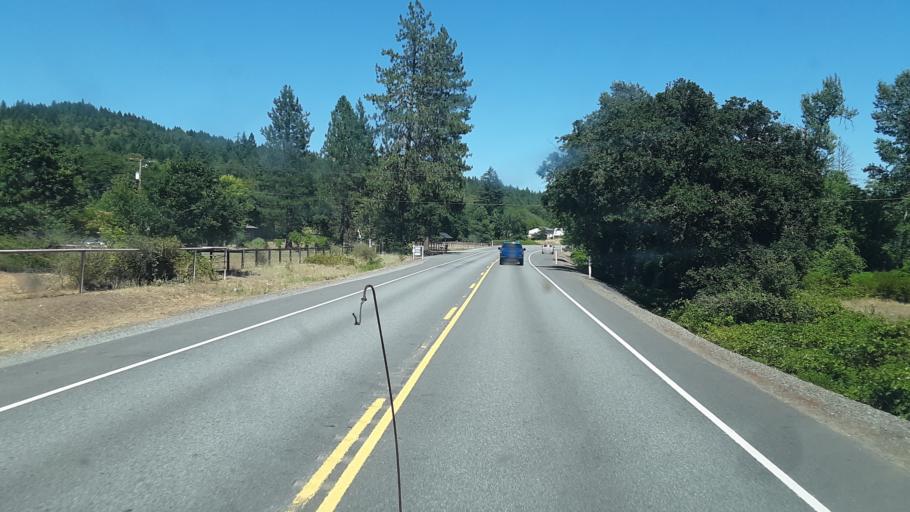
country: US
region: Oregon
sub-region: Josephine County
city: Redwood
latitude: 42.3825
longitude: -123.4857
